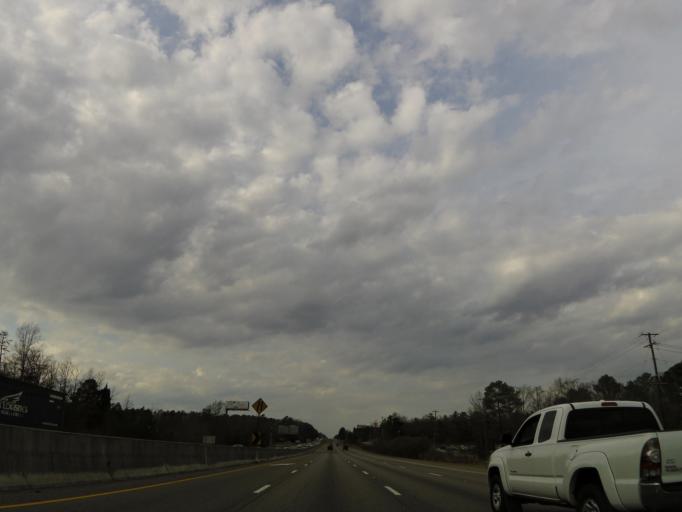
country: US
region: South Carolina
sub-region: Lexington County
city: Irmo
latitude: 34.1016
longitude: -81.1774
